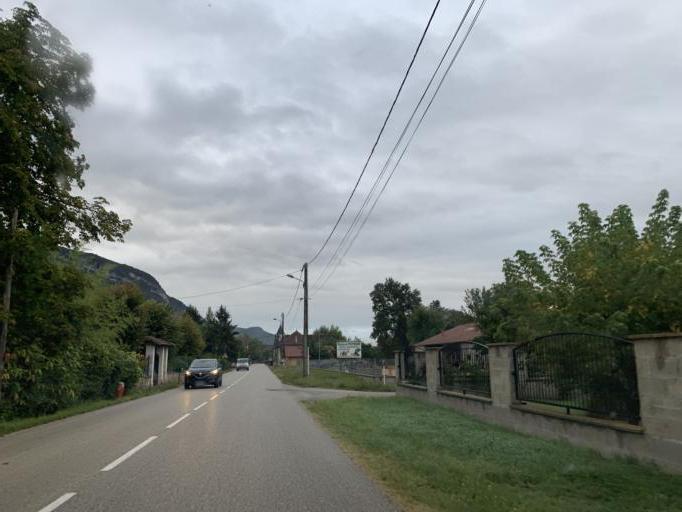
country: FR
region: Rhone-Alpes
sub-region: Departement de l'Isere
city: Les Avenieres
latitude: 45.6971
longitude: 5.5853
